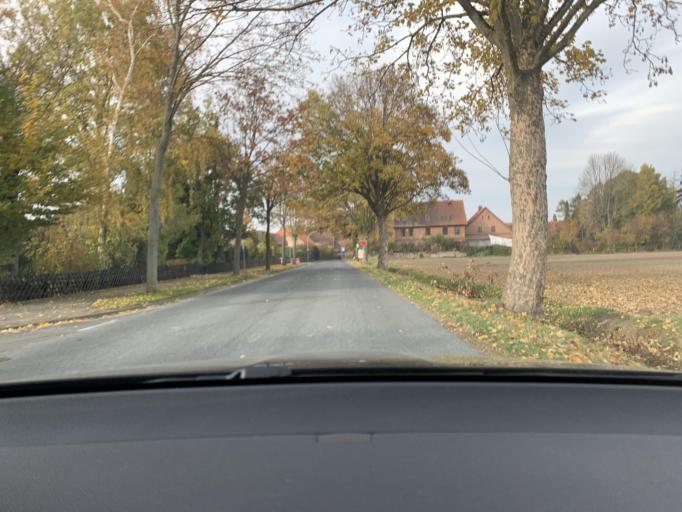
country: DE
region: Lower Saxony
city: Meine
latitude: 52.3786
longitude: 10.5455
